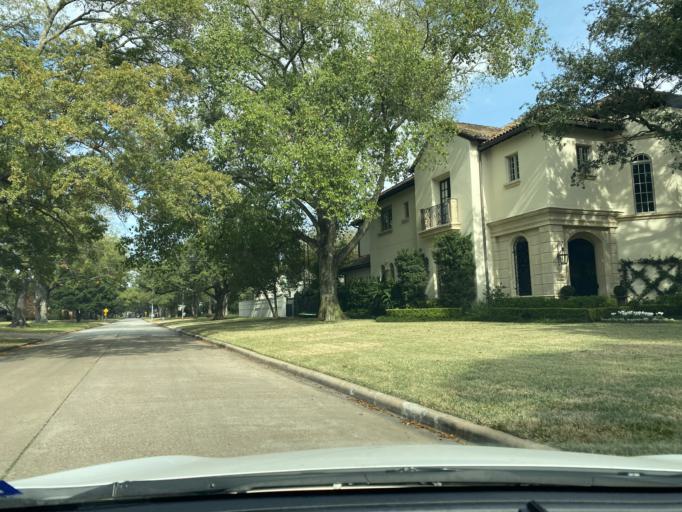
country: US
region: Texas
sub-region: Harris County
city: Hunters Creek Village
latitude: 29.7512
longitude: -95.4740
